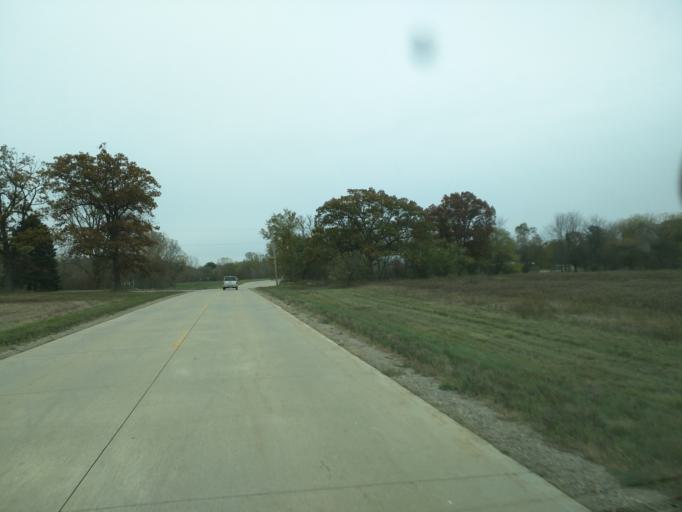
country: US
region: Michigan
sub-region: Ingham County
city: Edgemont Park
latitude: 42.7732
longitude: -84.5695
